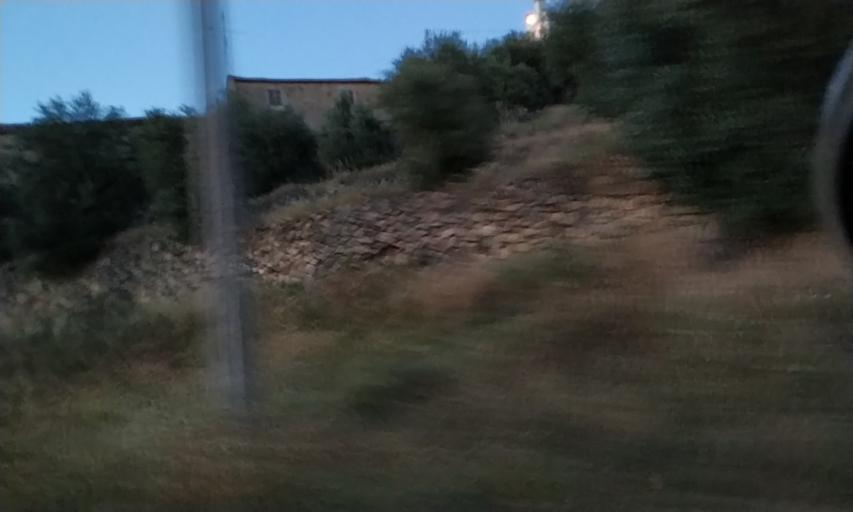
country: ES
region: Extremadura
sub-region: Provincia de Caceres
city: Piedras Albas
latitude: 39.8253
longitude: -6.9815
